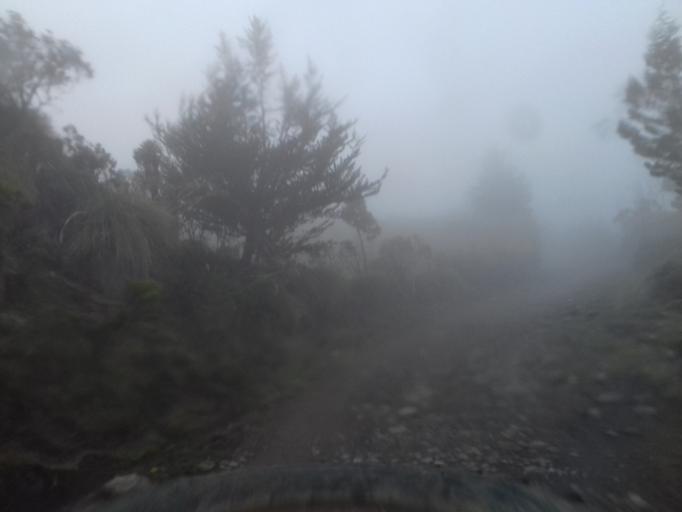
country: CO
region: Tolima
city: Murillo
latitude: 4.9043
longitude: -75.2535
